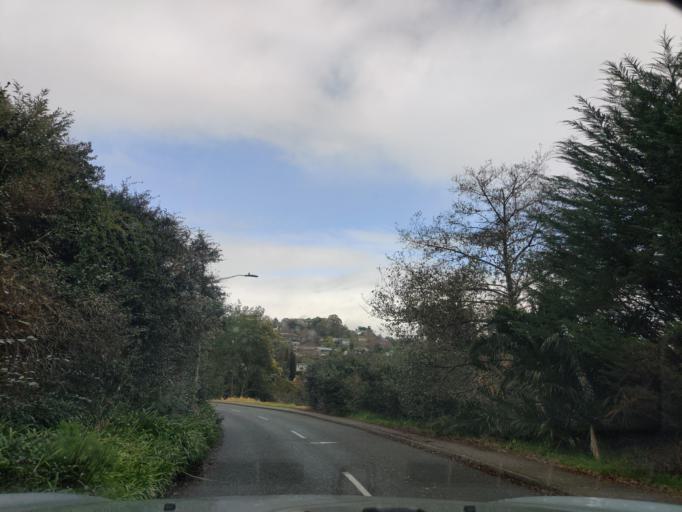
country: NZ
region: Hawke's Bay
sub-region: Hastings District
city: Hastings
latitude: -39.6743
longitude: 176.8944
